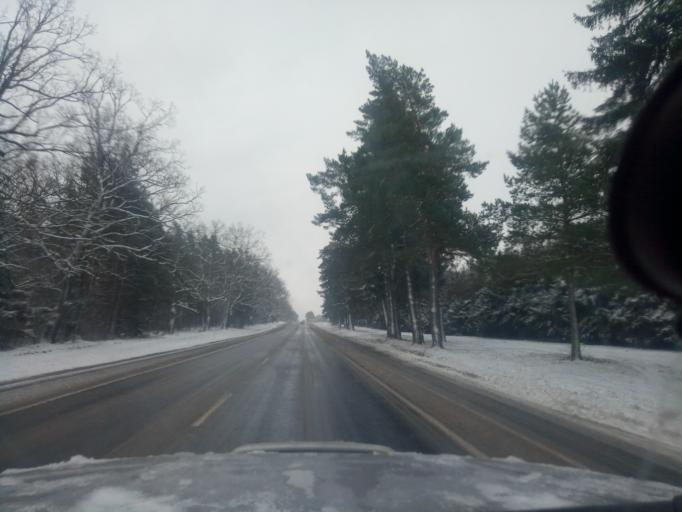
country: BY
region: Minsk
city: Haradzyeya
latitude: 53.2765
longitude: 26.5943
